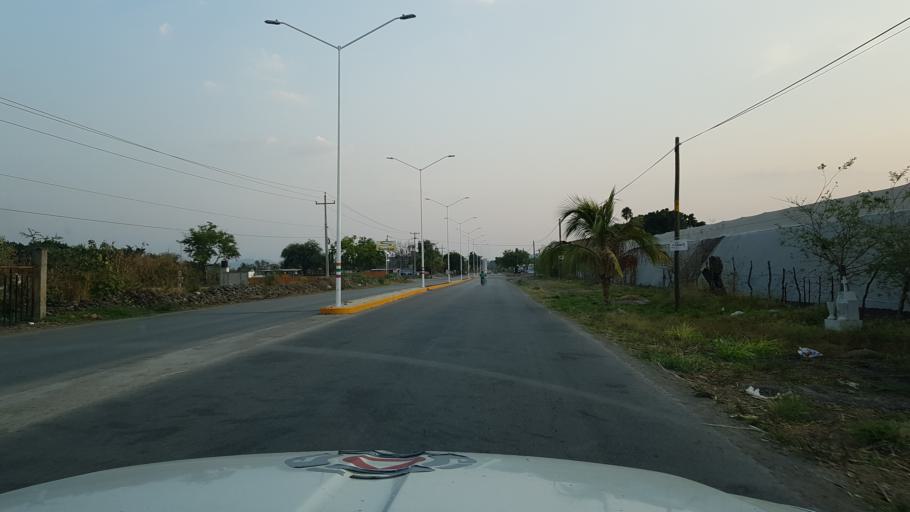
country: MX
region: Morelos
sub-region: Ayala
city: Abelardo L. Rodriguez
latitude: 18.7328
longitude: -98.9891
